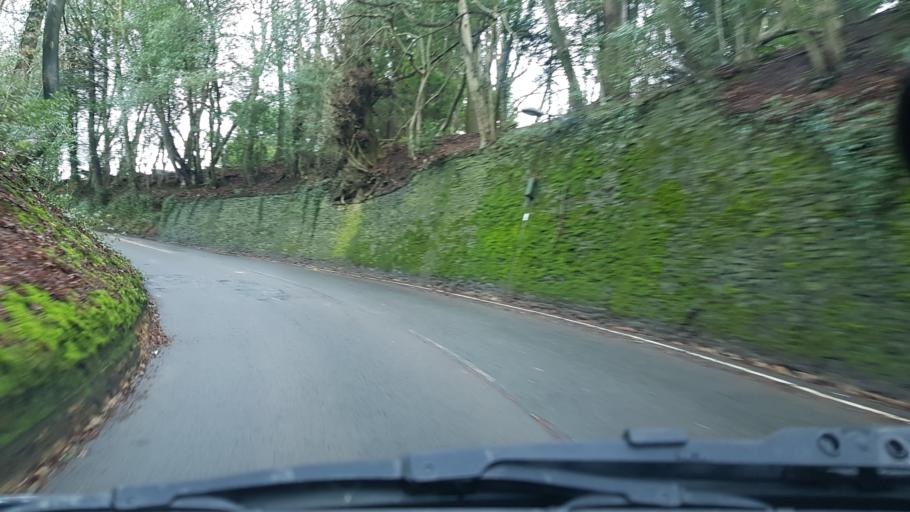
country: GB
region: England
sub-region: Surrey
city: Hindhead
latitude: 51.0899
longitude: -0.7482
